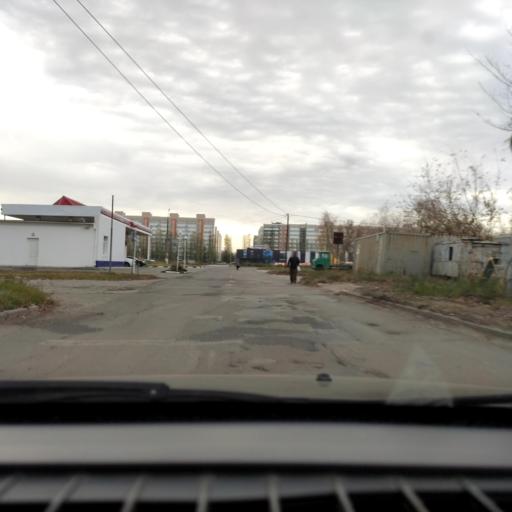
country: RU
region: Samara
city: Tol'yatti
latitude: 53.5522
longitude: 49.3134
